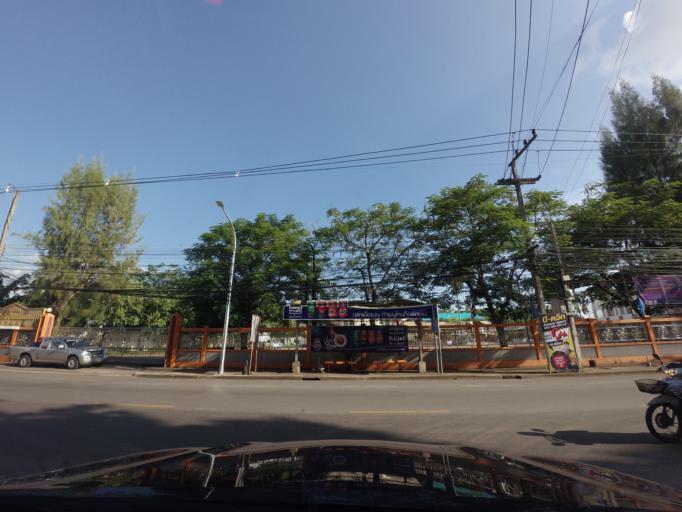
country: TH
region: Nong Khai
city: Nong Khai
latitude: 17.8827
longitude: 102.7485
